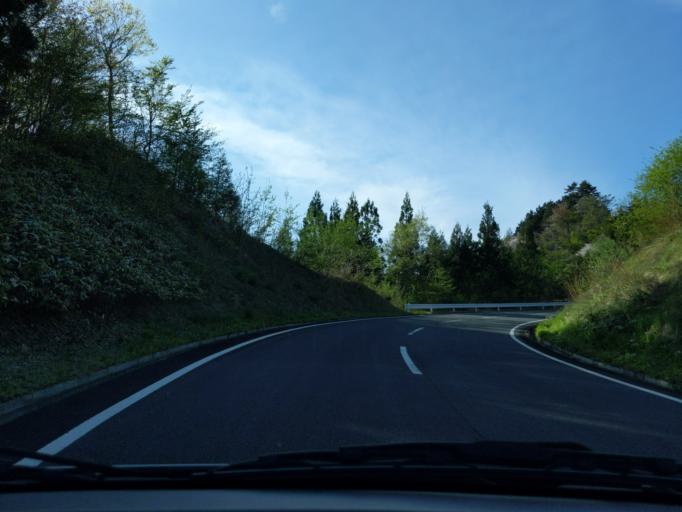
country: JP
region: Iwate
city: Ichinoseki
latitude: 38.8929
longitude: 140.8567
